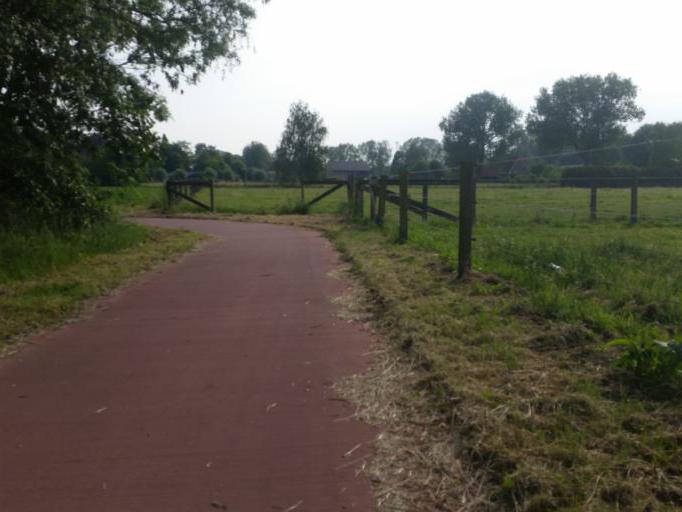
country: BE
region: Flanders
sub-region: Provincie Antwerpen
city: Lint
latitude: 51.1070
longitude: 4.4882
